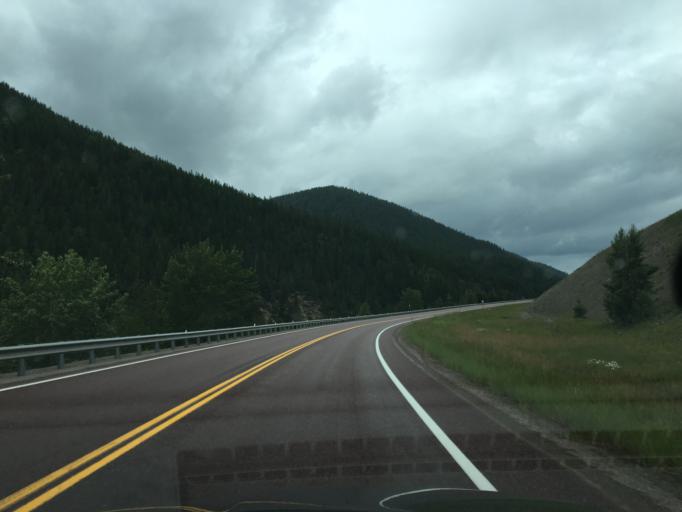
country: US
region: Montana
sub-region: Flathead County
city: Bigfork
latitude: 48.2348
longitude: -113.5670
